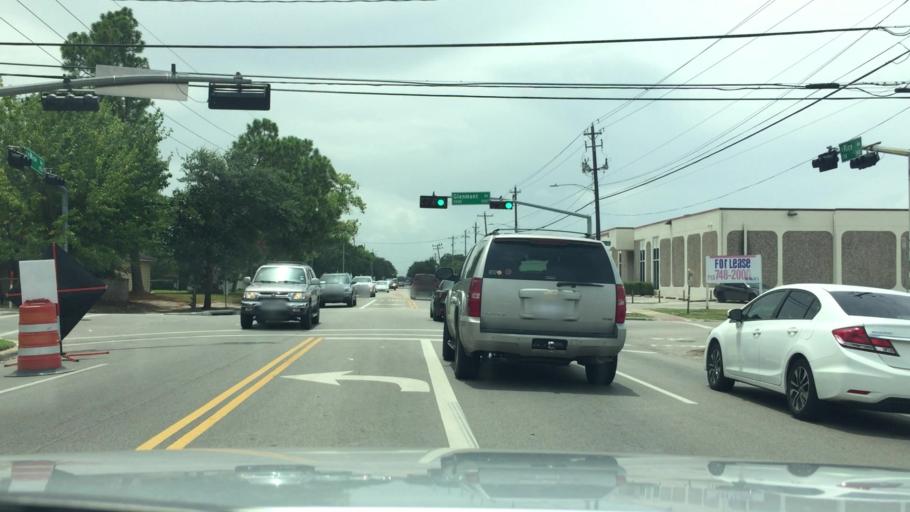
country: US
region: Texas
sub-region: Harris County
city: Bellaire
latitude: 29.7205
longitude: -95.4681
